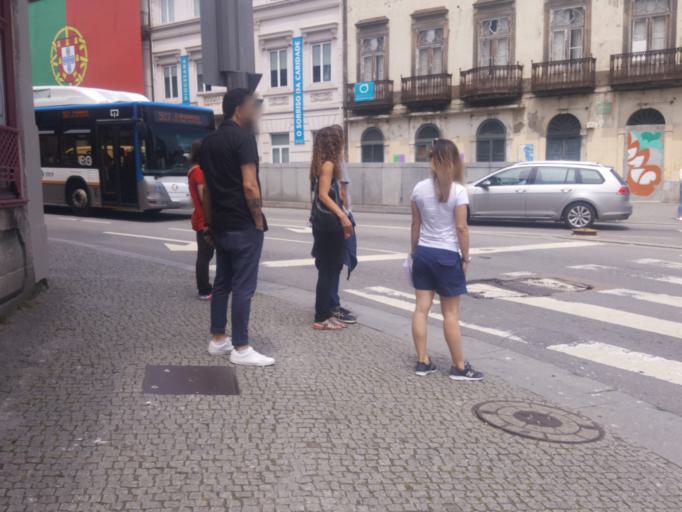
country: PT
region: Porto
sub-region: Porto
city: Porto
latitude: 41.1471
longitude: -8.6206
